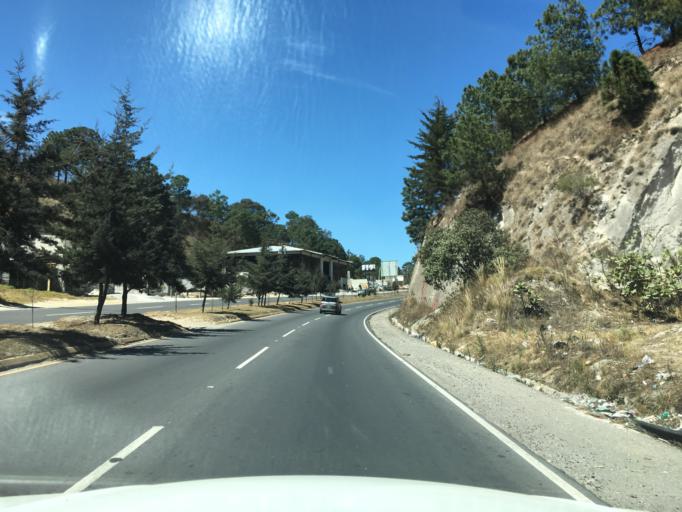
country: GT
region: Quetzaltenango
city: Salcaja
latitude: 14.8716
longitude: -91.4701
